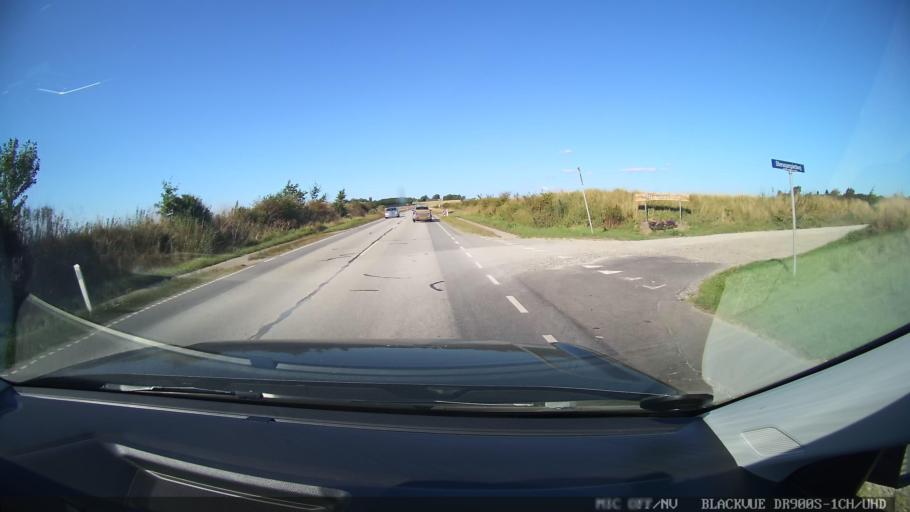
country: DK
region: Central Jutland
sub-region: Randers Kommune
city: Spentrup
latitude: 56.5184
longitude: 10.0145
